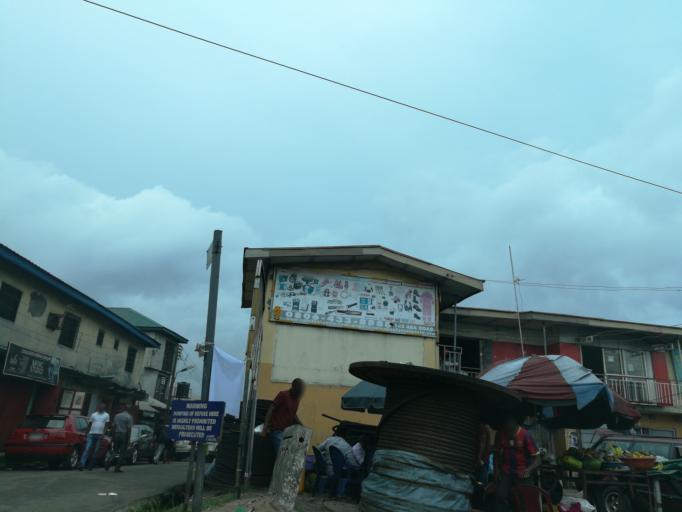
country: NG
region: Rivers
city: Port Harcourt
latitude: 4.8139
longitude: 7.0101
